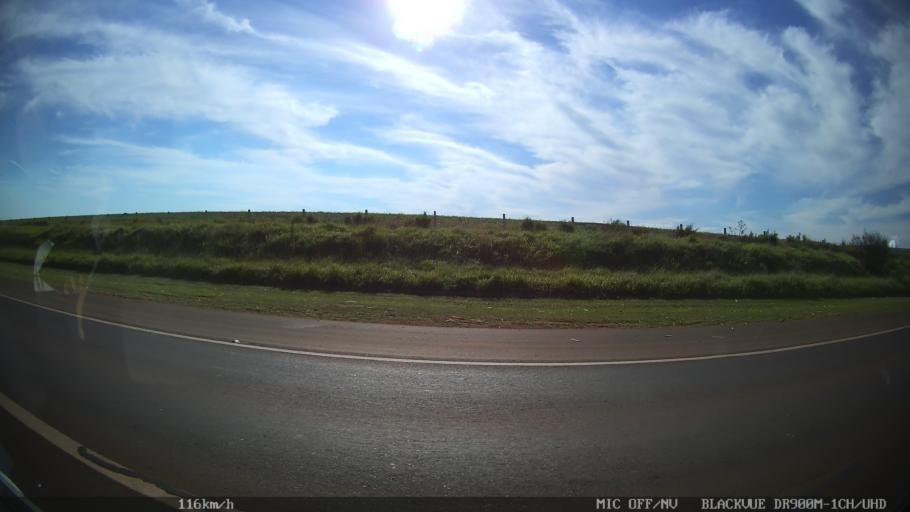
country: BR
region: Sao Paulo
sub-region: Americo Brasiliense
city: Americo Brasiliense
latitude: -21.7672
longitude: -48.0876
